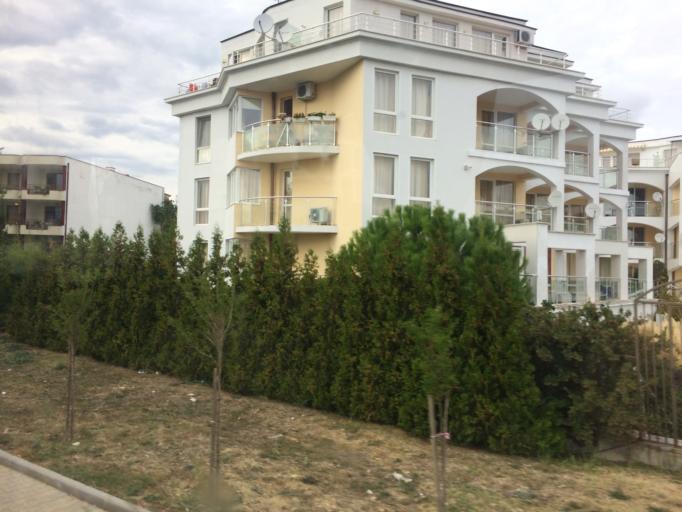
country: BG
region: Burgas
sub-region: Obshtina Nesebur
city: Sveti Vlas
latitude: 42.7112
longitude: 27.7619
